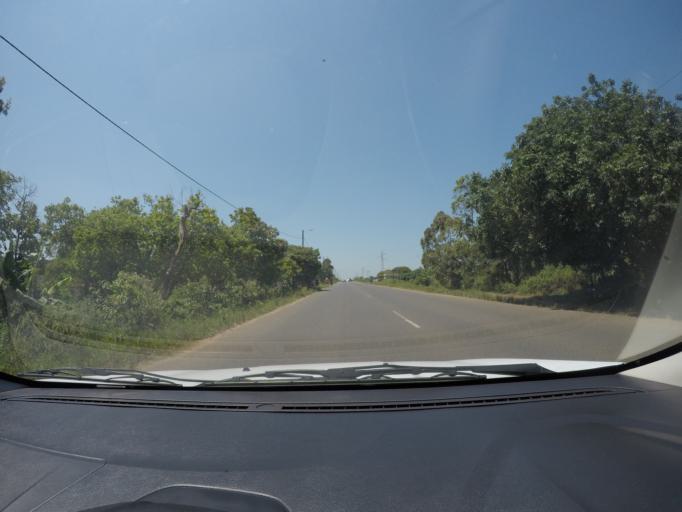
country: ZA
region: KwaZulu-Natal
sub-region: uThungulu District Municipality
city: eSikhawini
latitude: -28.8431
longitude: 31.9338
